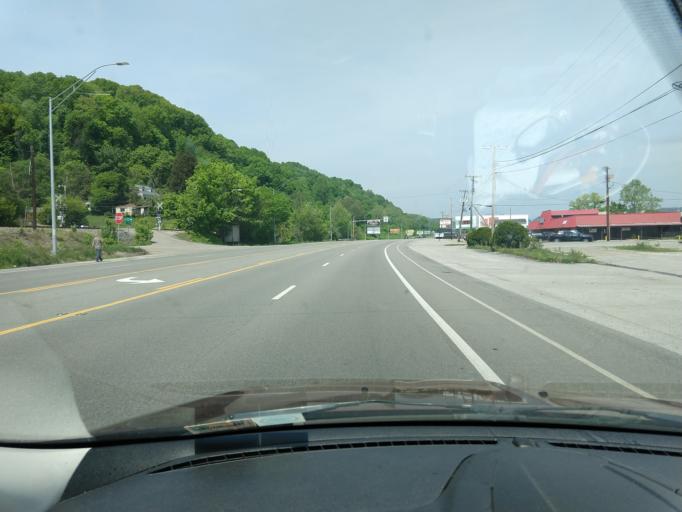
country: US
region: West Virginia
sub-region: Kanawha County
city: Dunbar
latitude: 38.3589
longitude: -81.7569
